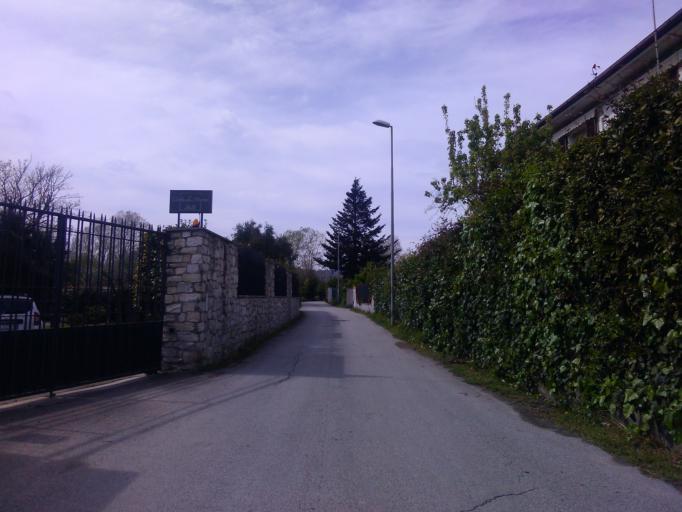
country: IT
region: Tuscany
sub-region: Provincia di Massa-Carrara
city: Marina di Carrara
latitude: 44.0483
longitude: 10.0228
